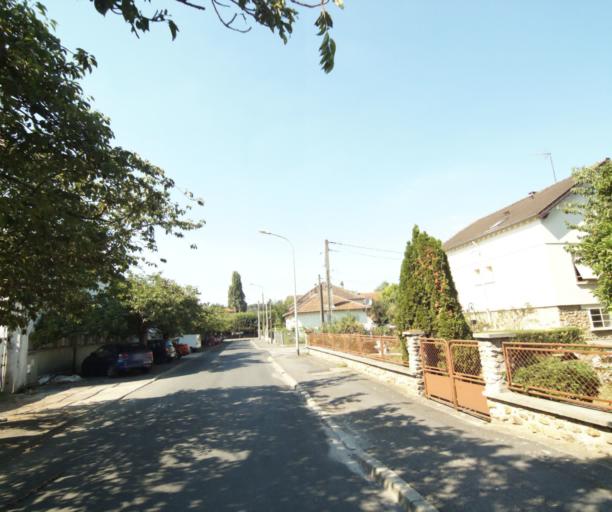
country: FR
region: Ile-de-France
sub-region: Departement de Seine-et-Marne
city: Pomponne
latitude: 48.8775
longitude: 2.6980
